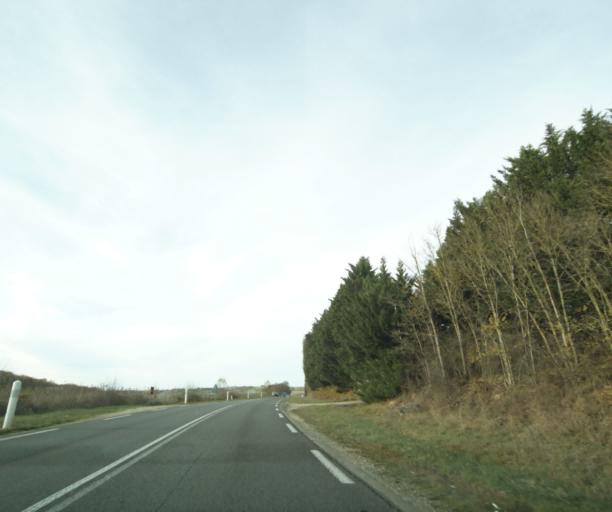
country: FR
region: Midi-Pyrenees
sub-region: Departement du Gers
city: Gimont
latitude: 43.6186
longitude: 0.9150
